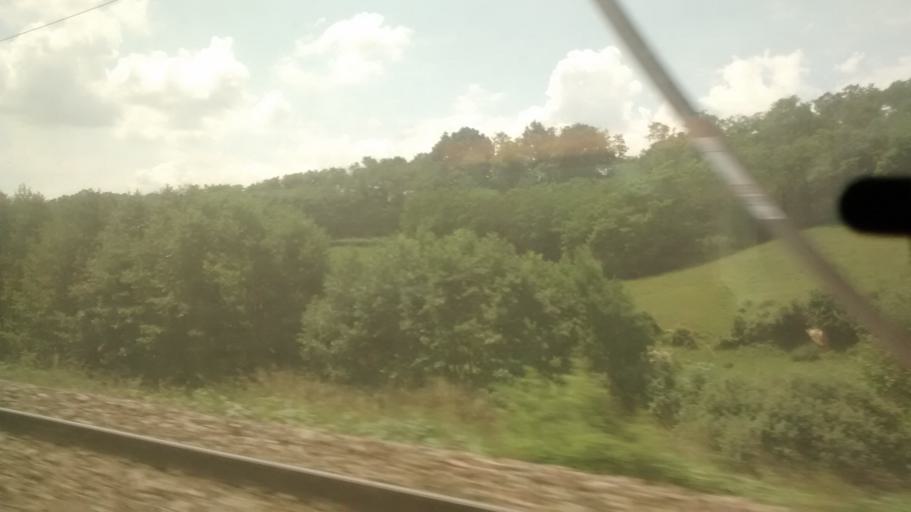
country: FR
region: Bourgogne
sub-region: Departement de Saone-et-Loire
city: Saint-Leu
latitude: 46.7061
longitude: 4.5345
